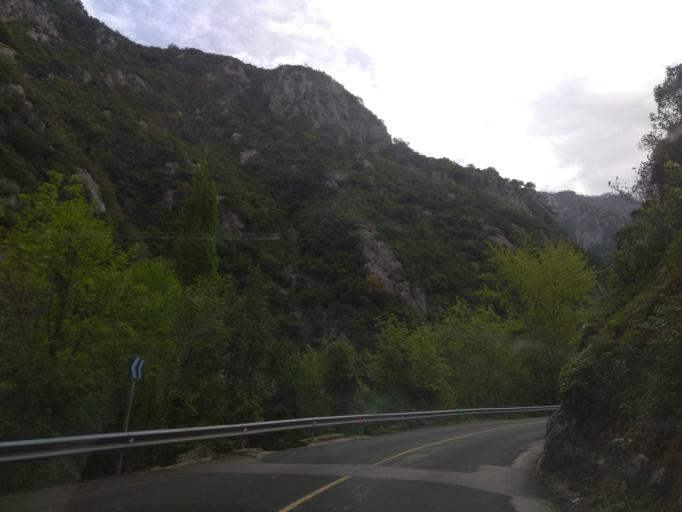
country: ES
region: Cantabria
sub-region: Provincia de Cantabria
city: Tresviso
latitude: 43.2483
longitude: -4.5923
